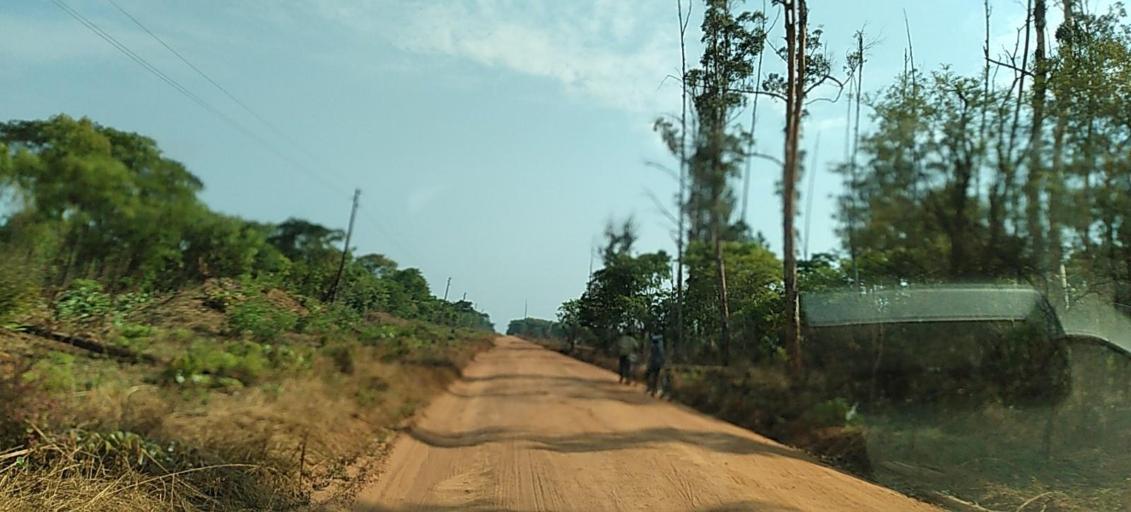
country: ZM
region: Copperbelt
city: Kalulushi
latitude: -12.9969
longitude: 27.8141
